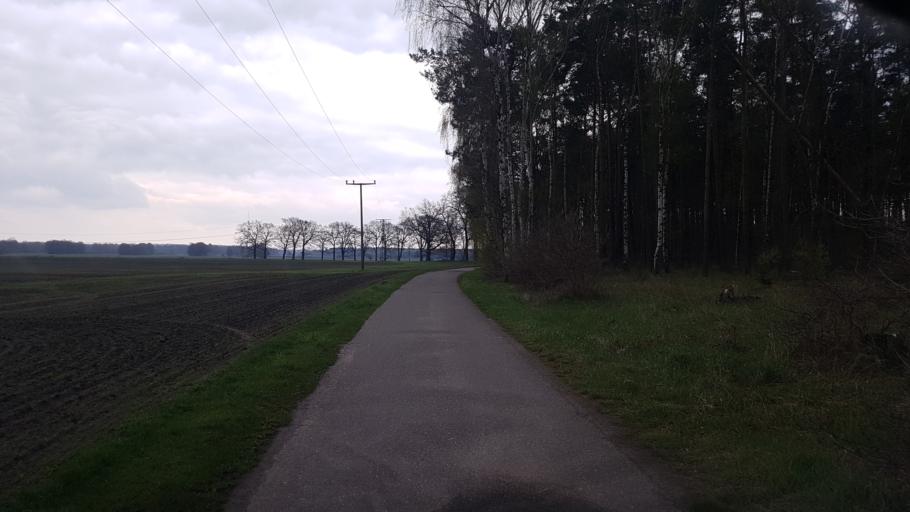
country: DE
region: Brandenburg
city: Bronkow
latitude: 51.6408
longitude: 13.8963
